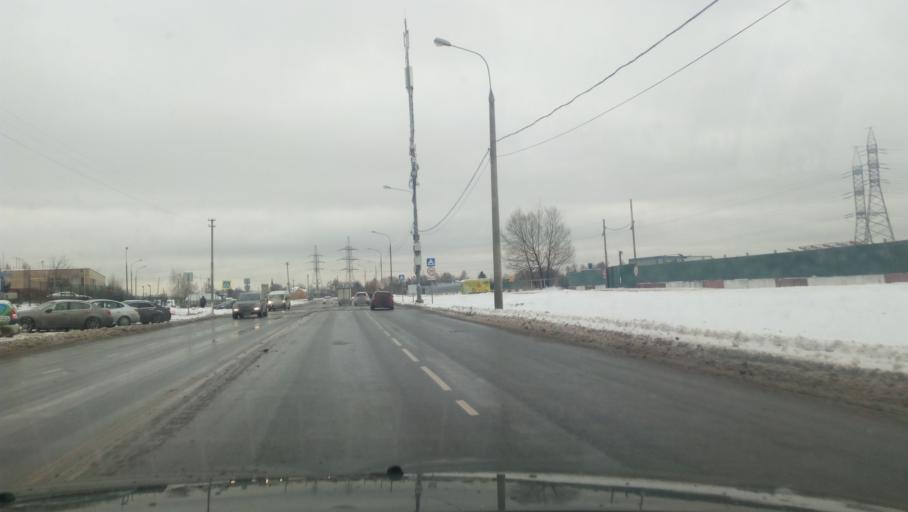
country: RU
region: Moscow
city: Zhulebino
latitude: 55.7281
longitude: 37.8599
